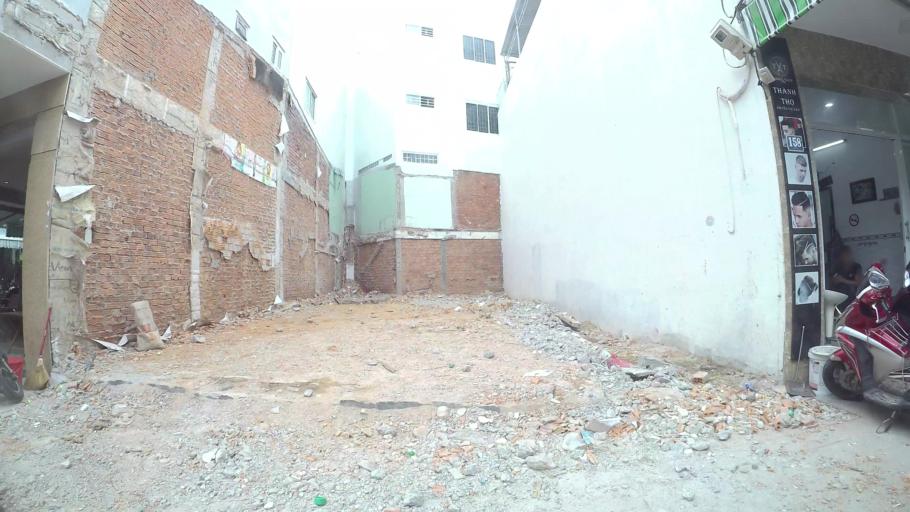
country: VN
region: Da Nang
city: Da Nang
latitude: 16.0778
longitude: 108.2150
